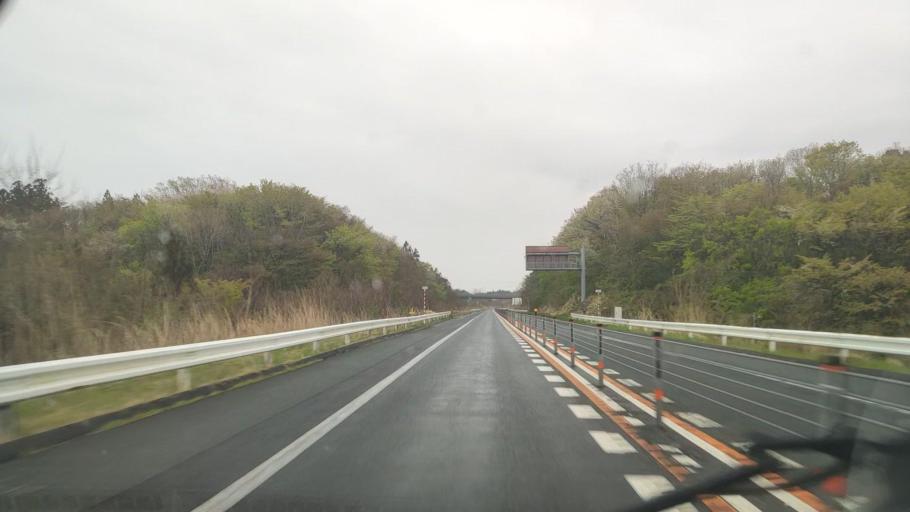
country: JP
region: Akita
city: Noshiromachi
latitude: 40.1489
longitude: 140.0209
